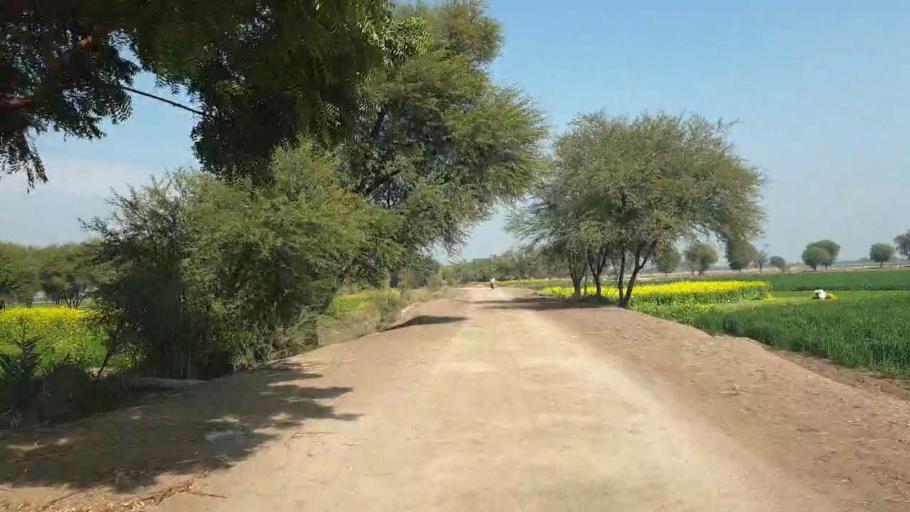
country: PK
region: Sindh
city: Shahdadpur
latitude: 25.9937
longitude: 68.5335
